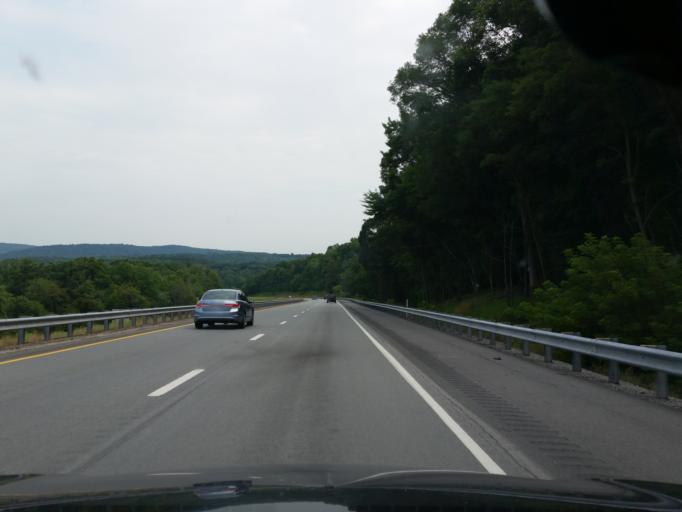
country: US
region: Pennsylvania
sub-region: Perry County
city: Newport
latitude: 40.5068
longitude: -77.1275
